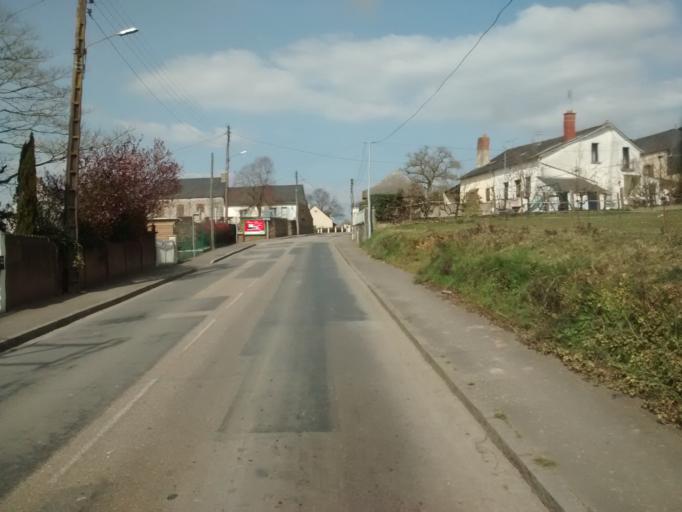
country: FR
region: Brittany
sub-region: Departement d'Ille-et-Vilaine
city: Grand-Fougeray
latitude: 47.7262
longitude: -1.7284
